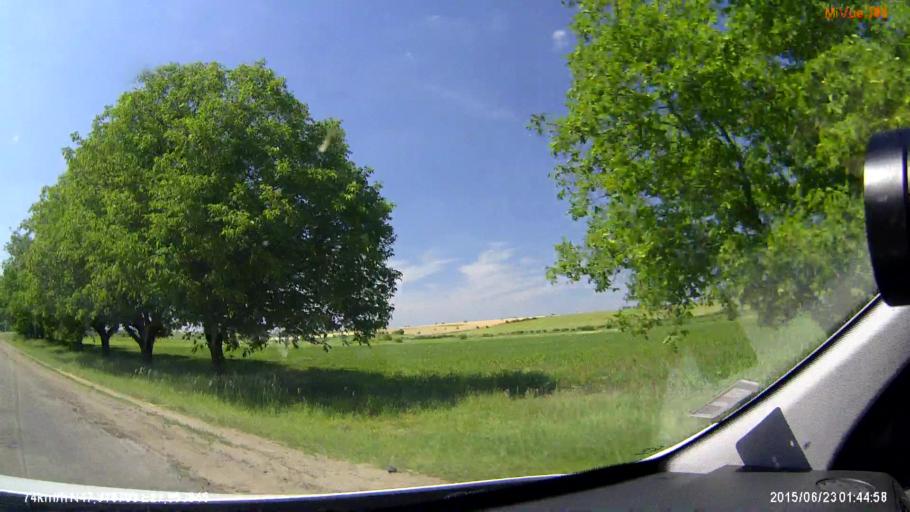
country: RO
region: Iasi
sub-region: Comuna Victoria
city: Victoria
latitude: 47.3186
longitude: 27.6533
